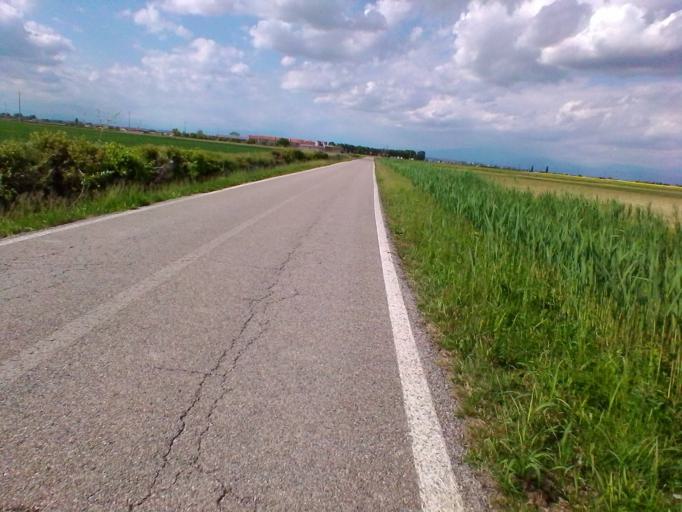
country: IT
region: Veneto
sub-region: Provincia di Verona
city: Pradelle
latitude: 45.2671
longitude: 10.8311
